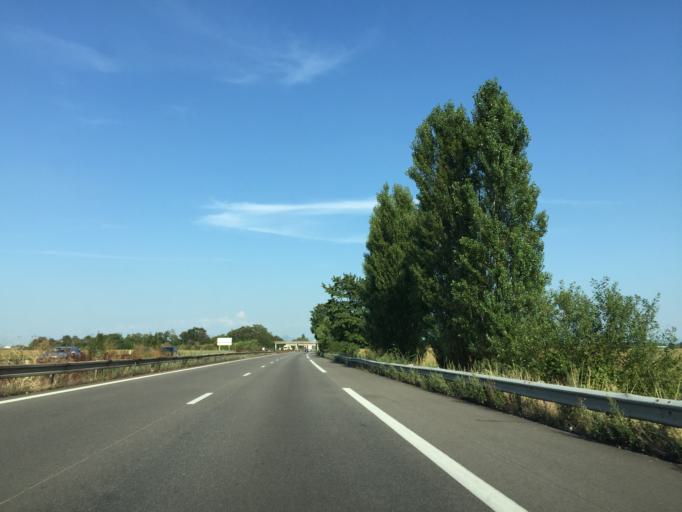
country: FR
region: Alsace
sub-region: Departement du Bas-Rhin
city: Geispolsheim
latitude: 48.5244
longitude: 7.6539
